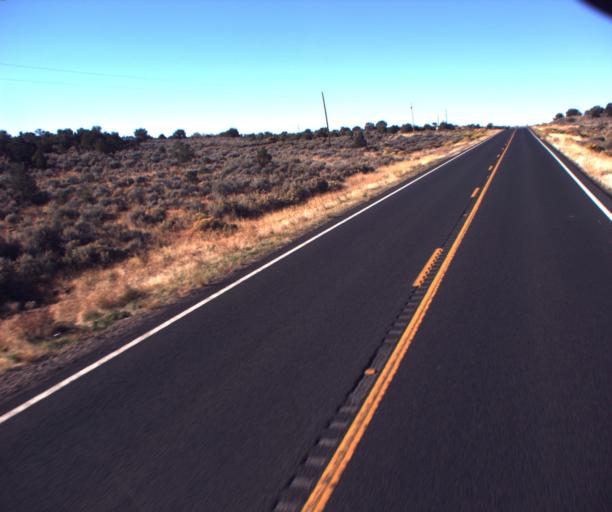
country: US
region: Arizona
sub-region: Apache County
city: Ganado
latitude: 35.7677
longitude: -109.7452
